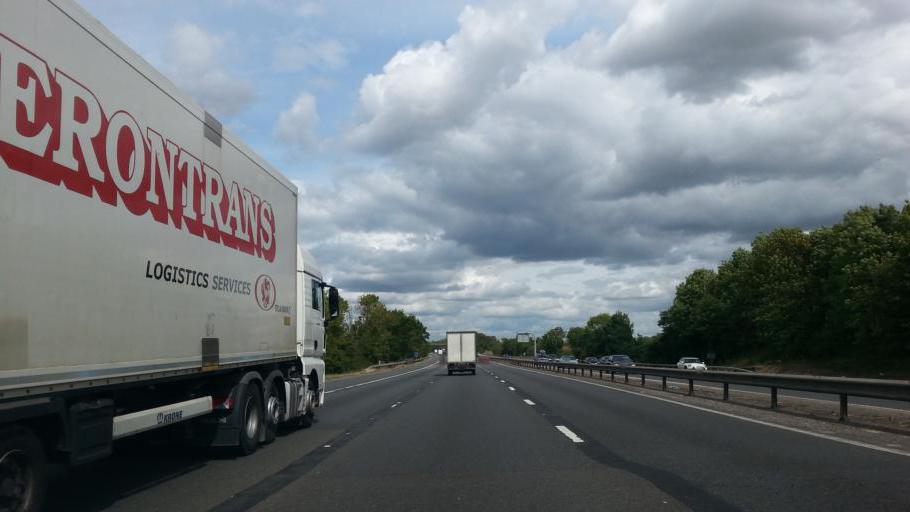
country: GB
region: England
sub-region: Hertfordshire
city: Sawbridgeworth
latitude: 51.7716
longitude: 0.1595
